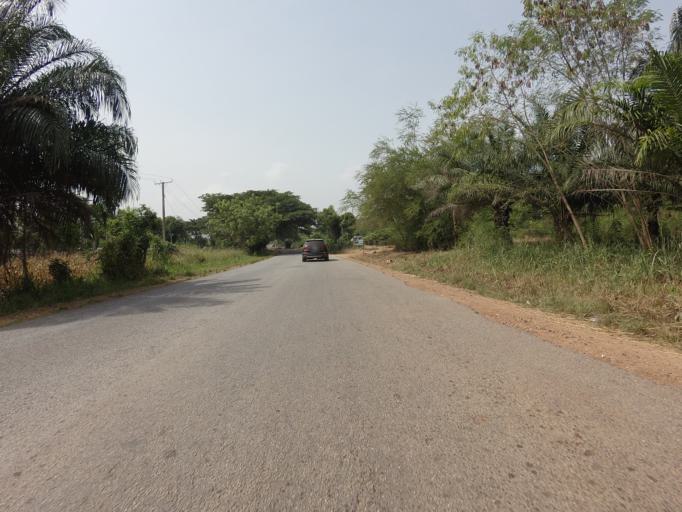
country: GH
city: Akropong
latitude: 6.2401
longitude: 0.1055
